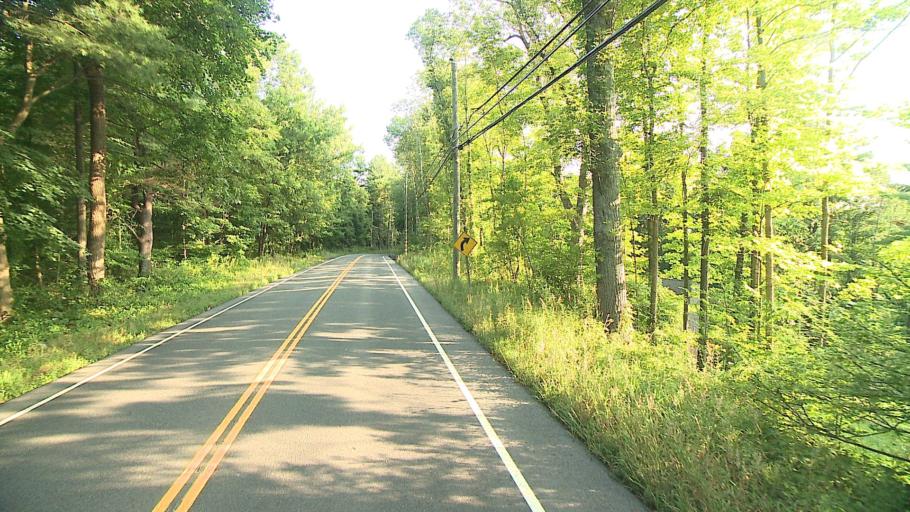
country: US
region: Connecticut
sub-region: Fairfield County
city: Sherman
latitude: 41.6020
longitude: -73.4591
